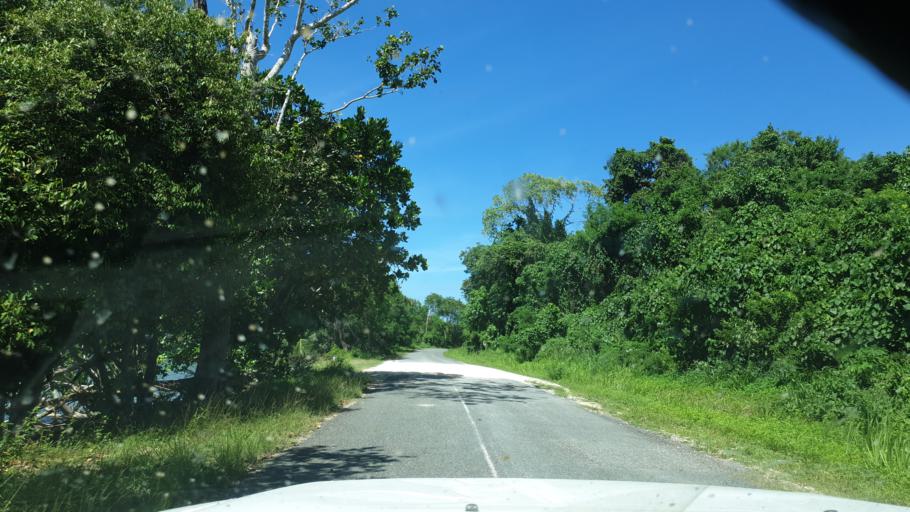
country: PG
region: Madang
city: Madang
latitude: -4.4954
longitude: 145.4261
